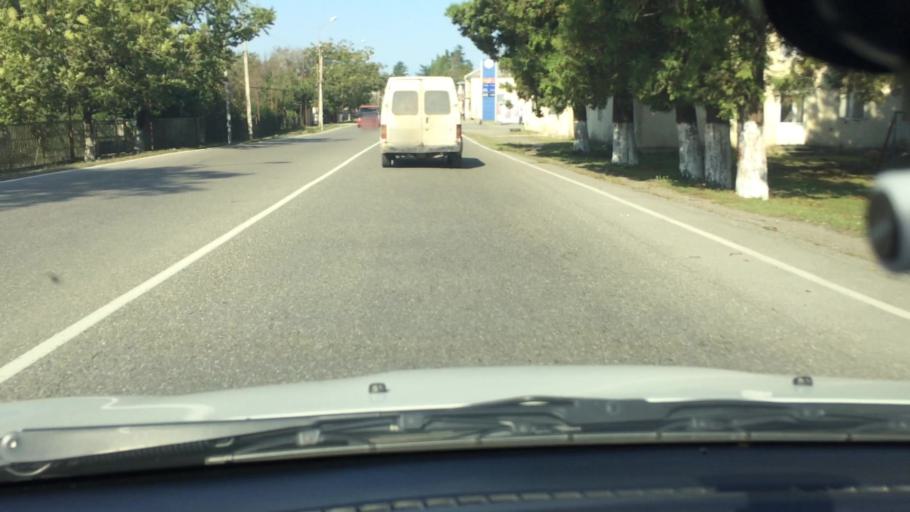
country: GE
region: Guria
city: Lanchkhuti
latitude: 42.0843
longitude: 42.0430
